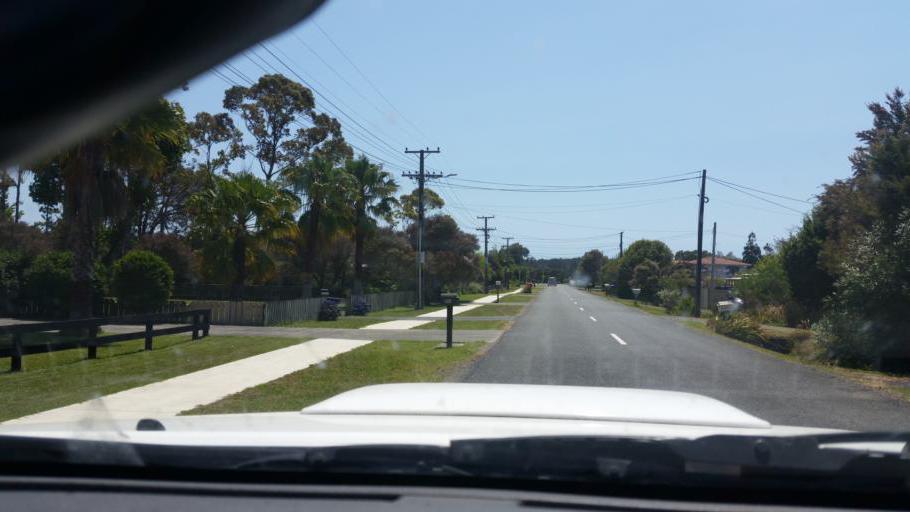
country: NZ
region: Auckland
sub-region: Auckland
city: Wellsford
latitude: -36.1227
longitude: 174.5748
